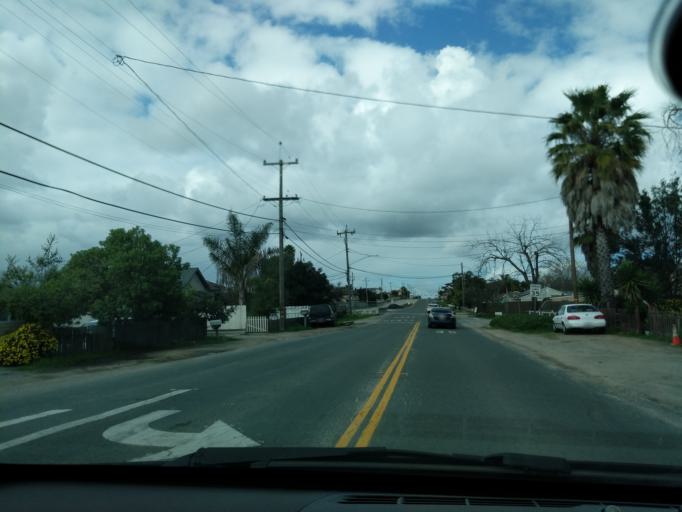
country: US
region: California
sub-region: Monterey County
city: Boronda
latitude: 36.7304
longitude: -121.6416
